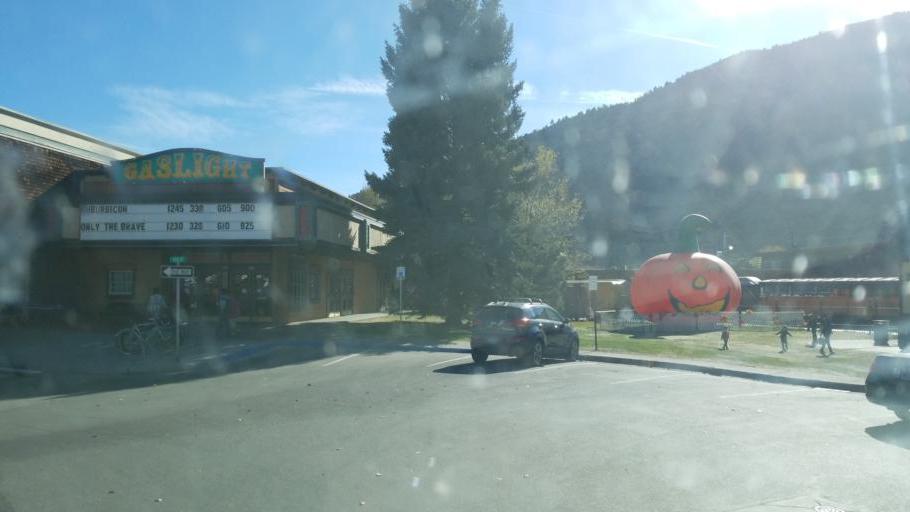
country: US
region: Colorado
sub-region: La Plata County
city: Durango
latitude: 37.2692
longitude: -107.8822
